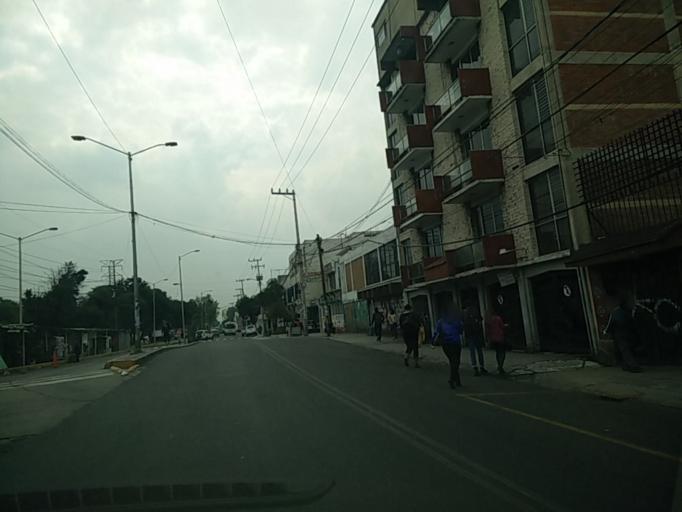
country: MX
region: Mexico
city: Colonia Lindavista
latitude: 19.4856
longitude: -99.1263
